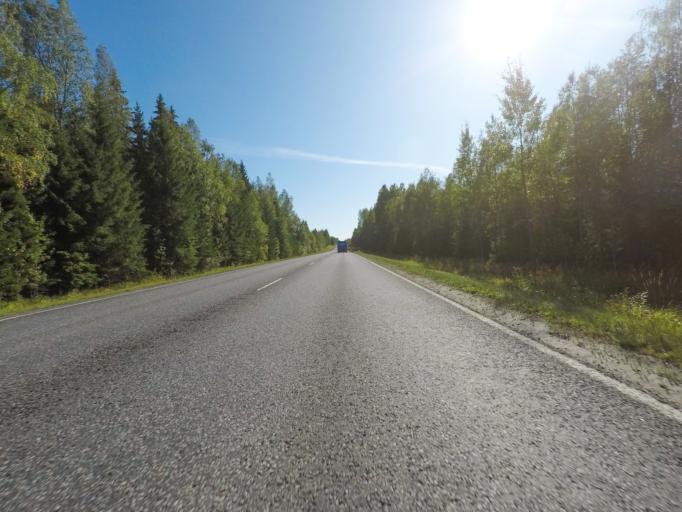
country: FI
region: Southern Savonia
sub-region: Pieksaemaeki
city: Joroinen
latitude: 62.0963
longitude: 27.8291
